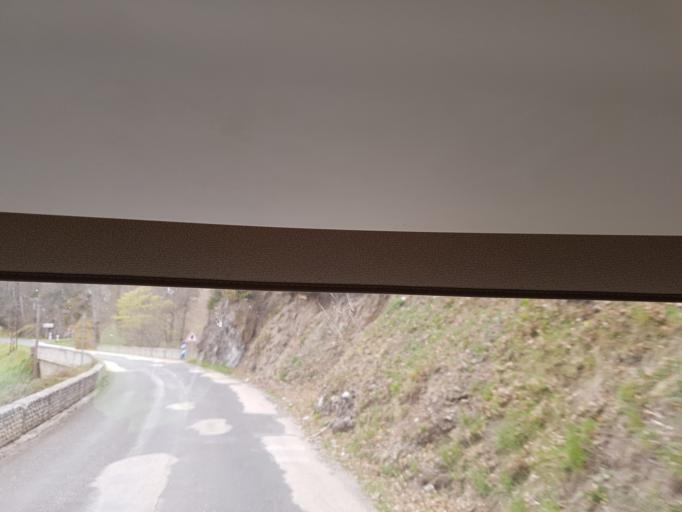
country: FR
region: Languedoc-Roussillon
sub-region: Departement de l'Aude
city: Quillan
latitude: 42.7522
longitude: 2.0854
